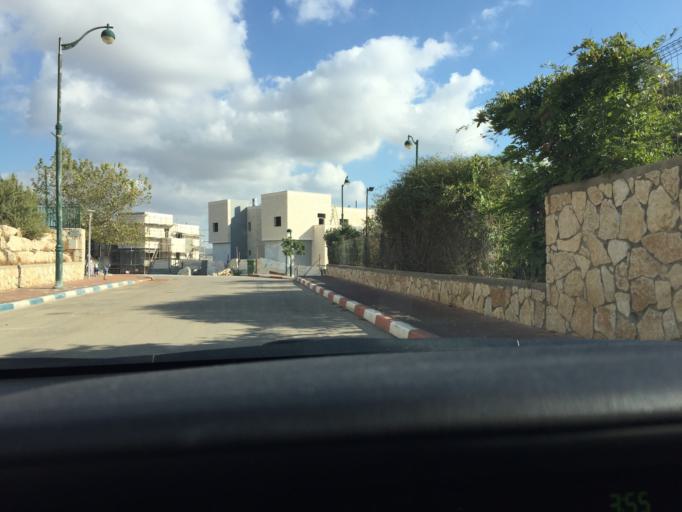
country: PS
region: West Bank
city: Rafat
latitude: 32.0636
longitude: 35.0537
